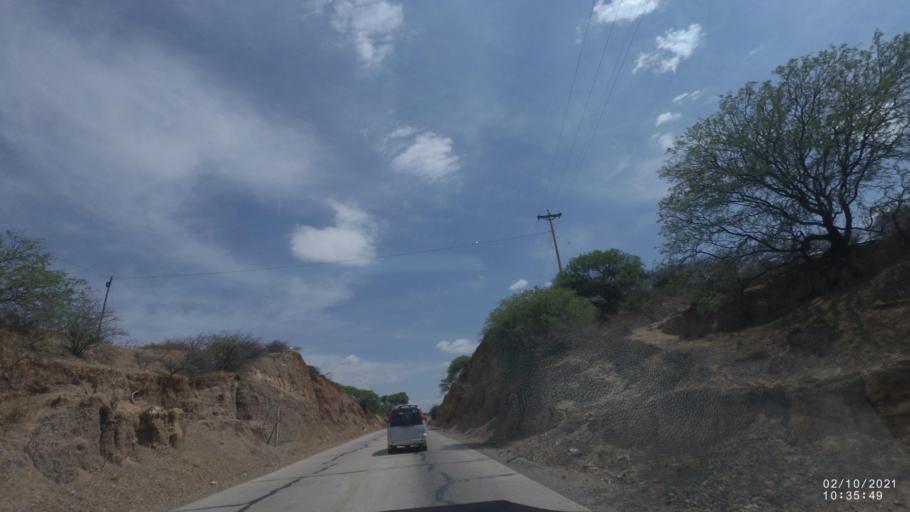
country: BO
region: Cochabamba
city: Capinota
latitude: -17.6570
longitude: -66.2586
